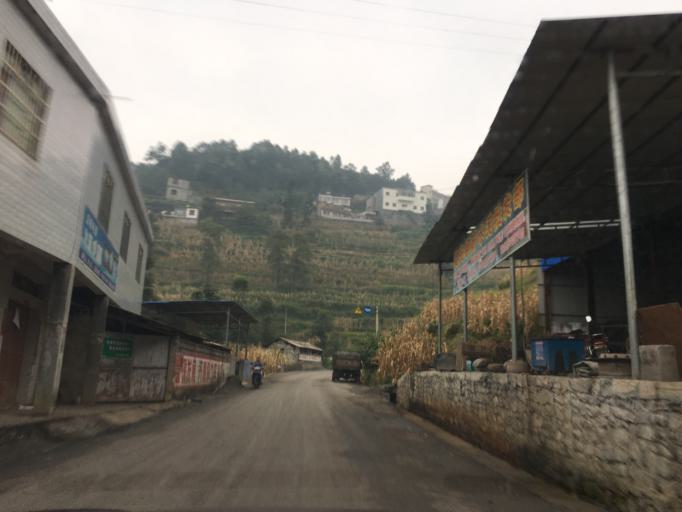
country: CN
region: Guizhou Sheng
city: Liupanshui
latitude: 26.0642
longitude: 105.1353
